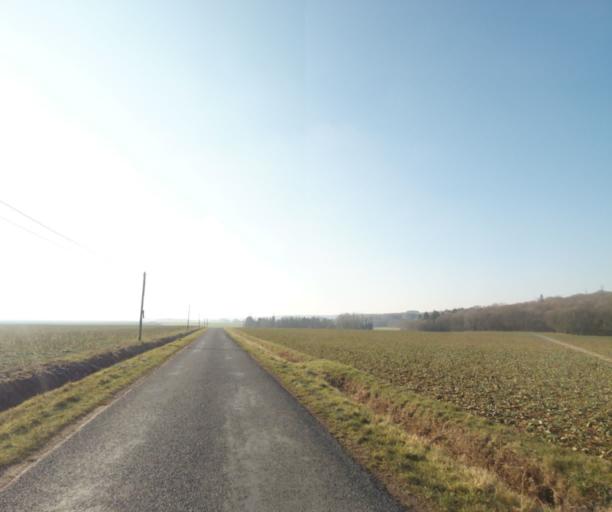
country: FR
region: Champagne-Ardenne
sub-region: Departement de la Haute-Marne
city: Bienville
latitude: 48.5369
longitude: 5.0152
